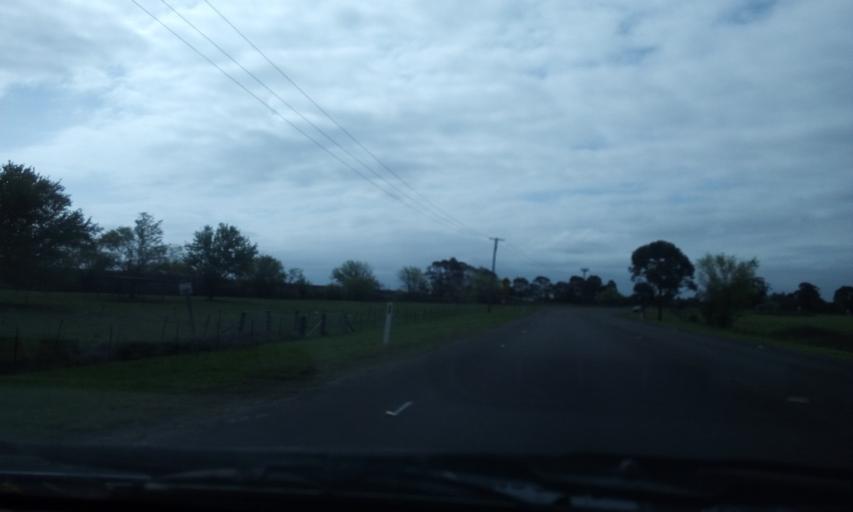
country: AU
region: New South Wales
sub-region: Campbelltown Municipality
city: Glen Alpine
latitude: -34.1154
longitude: 150.7442
